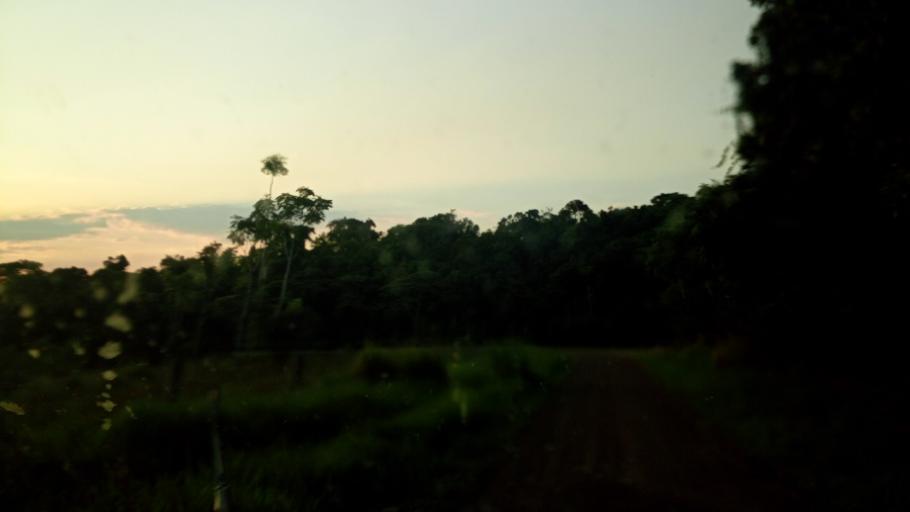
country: AU
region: Queensland
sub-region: Tablelands
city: Atherton
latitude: -17.3649
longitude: 145.7500
